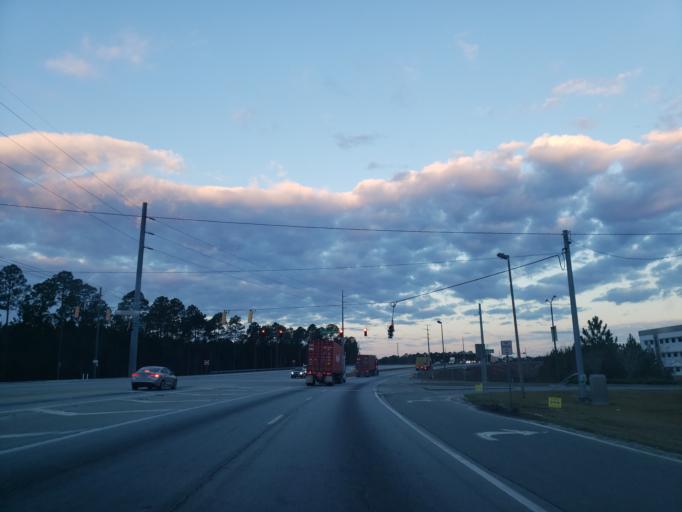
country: US
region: Georgia
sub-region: Chatham County
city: Port Wentworth
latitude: 32.1632
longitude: -81.2102
